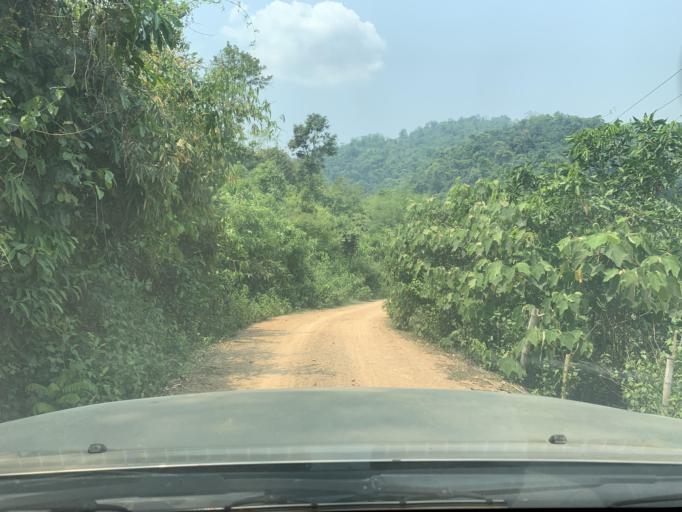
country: LA
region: Louangphabang
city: Louangphabang
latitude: 19.9691
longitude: 102.1262
